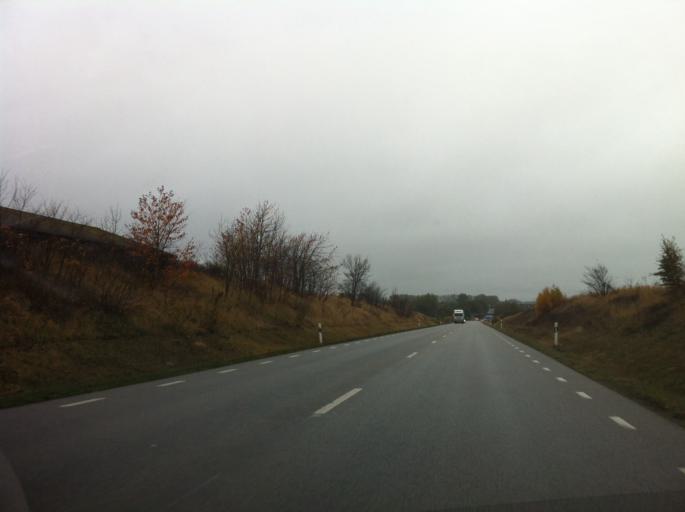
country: SE
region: Skane
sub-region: Kavlinge Kommun
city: Kaevlinge
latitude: 55.7845
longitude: 13.1331
